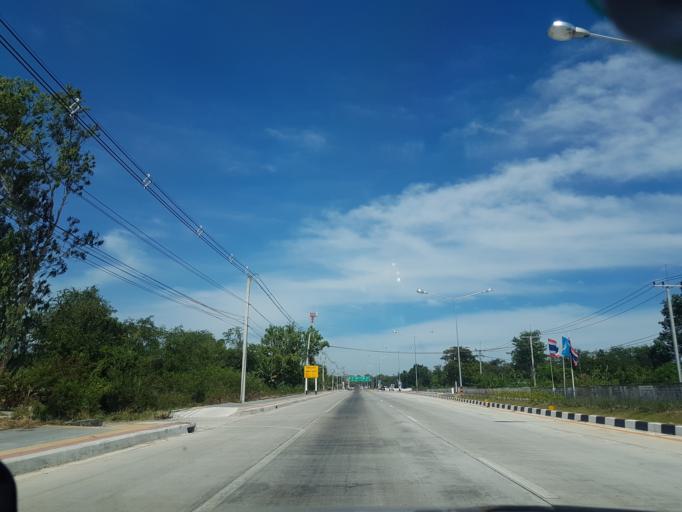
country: TH
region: Chon Buri
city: Sattahip
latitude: 12.6832
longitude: 100.9785
